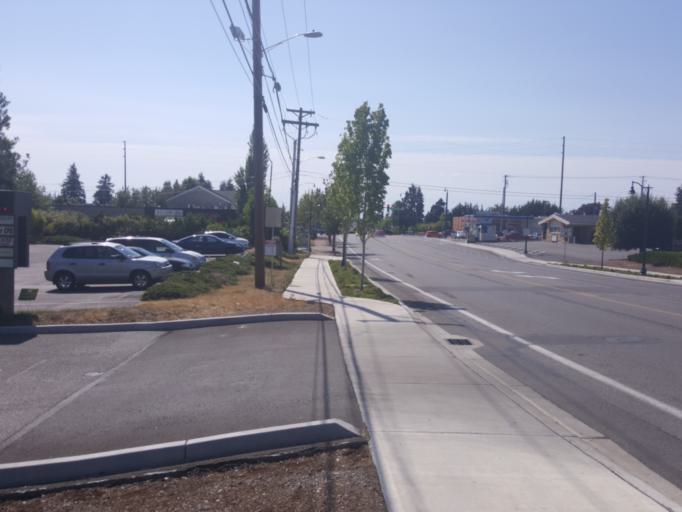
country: US
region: Washington
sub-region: Pierce County
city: University Place
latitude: 47.2353
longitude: -122.5349
